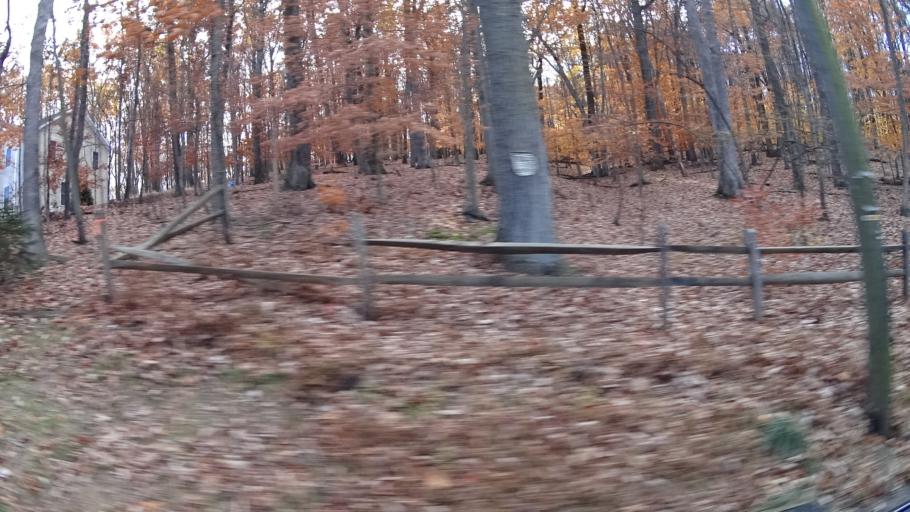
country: US
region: New Jersey
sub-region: Morris County
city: Mendham
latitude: 40.7706
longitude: -74.5675
